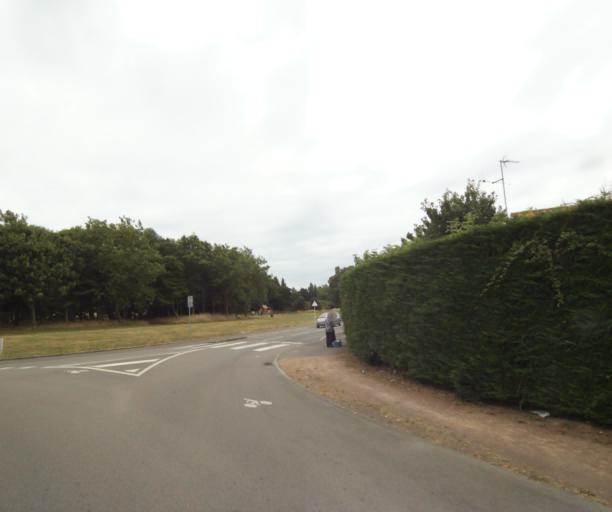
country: FR
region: Pays de la Loire
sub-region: Departement de la Vendee
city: Chateau-d'Olonne
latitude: 46.4924
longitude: -1.7462
